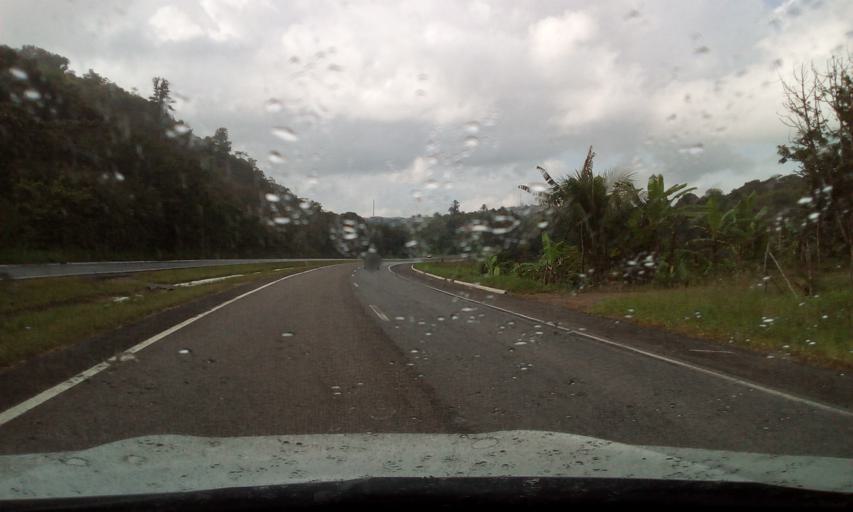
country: BR
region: Pernambuco
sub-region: Cabo De Santo Agostinho
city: Cabo
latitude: -8.2753
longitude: -35.0539
